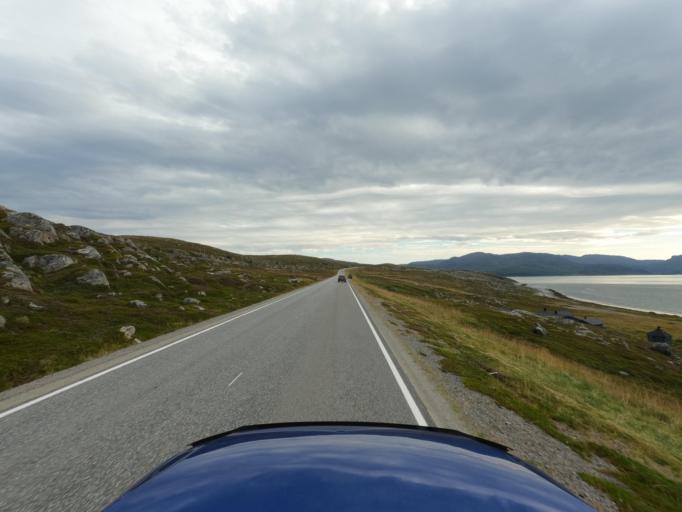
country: NO
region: Finnmark Fylke
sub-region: Hammerfest
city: Rypefjord
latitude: 70.5213
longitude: 23.7571
